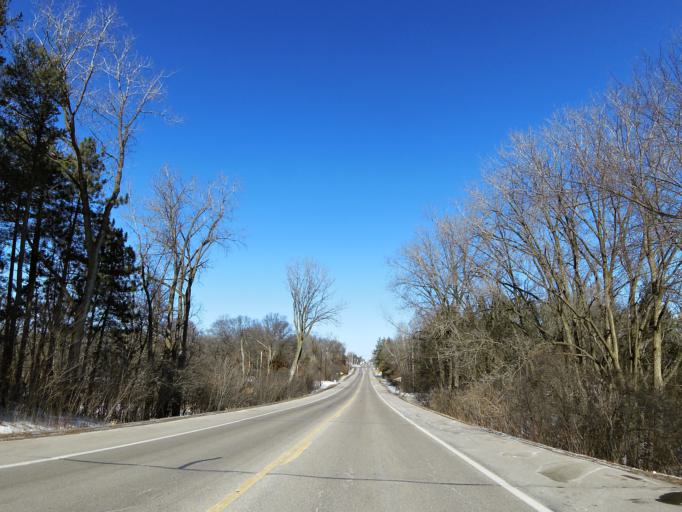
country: US
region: Minnesota
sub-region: Washington County
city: Lake Elmo
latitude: 45.0304
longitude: -92.8833
